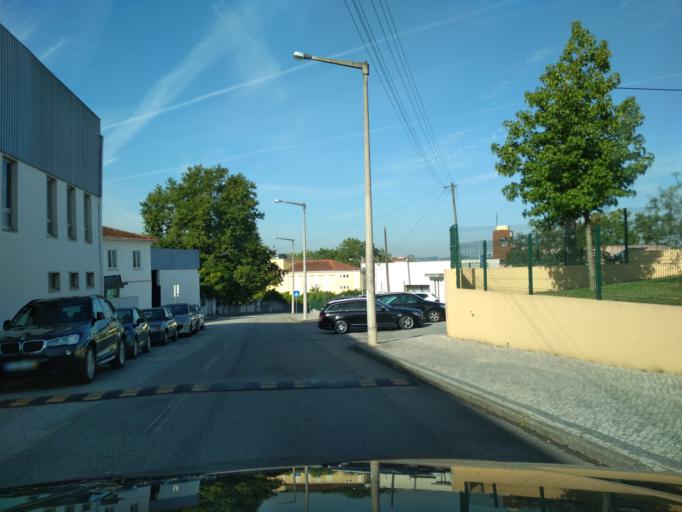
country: PT
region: Aveiro
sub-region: Mealhada
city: Mealhada
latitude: 40.3761
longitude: -8.4476
